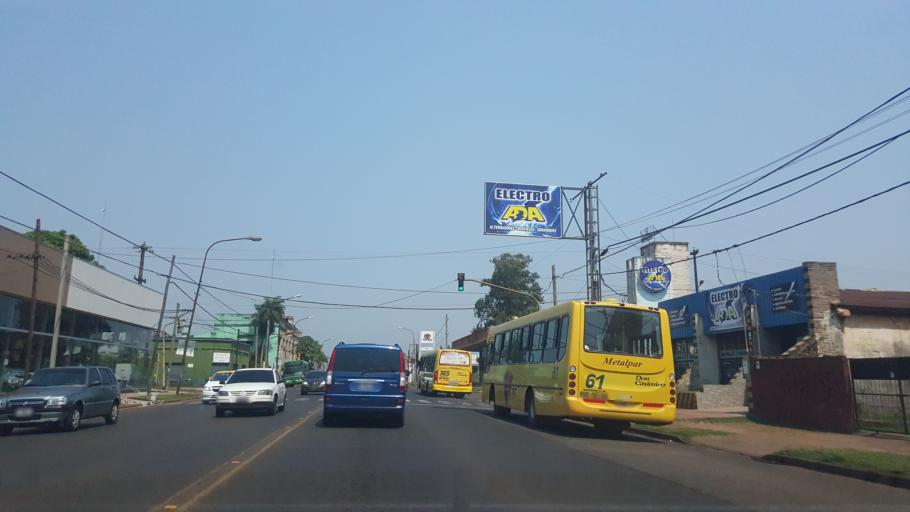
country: AR
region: Misiones
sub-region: Departamento de Capital
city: Posadas
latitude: -27.3972
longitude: -55.9017
